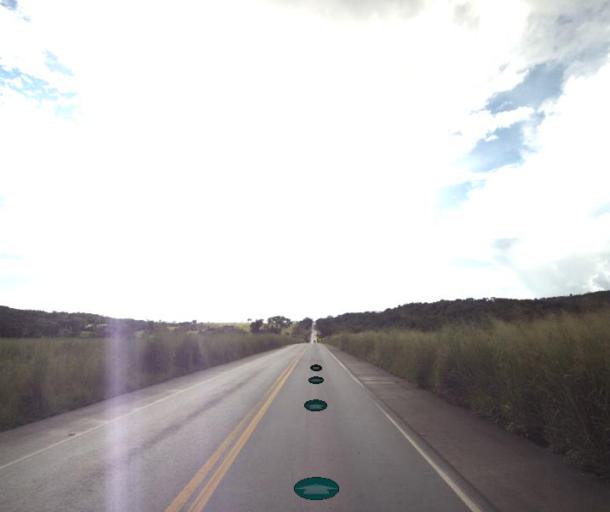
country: BR
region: Goias
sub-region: Jaragua
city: Jaragua
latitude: -15.6518
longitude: -49.3643
